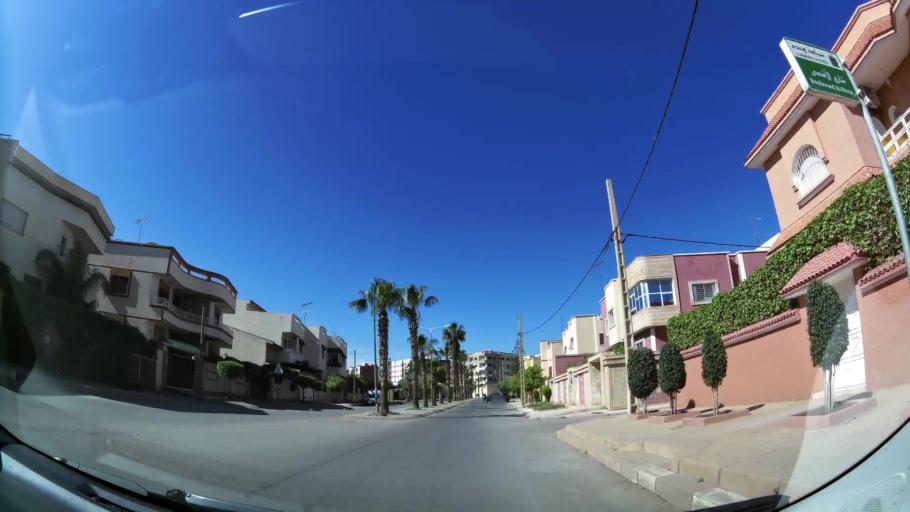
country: MA
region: Oriental
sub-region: Oujda-Angad
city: Oujda
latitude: 34.6607
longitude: -1.8957
